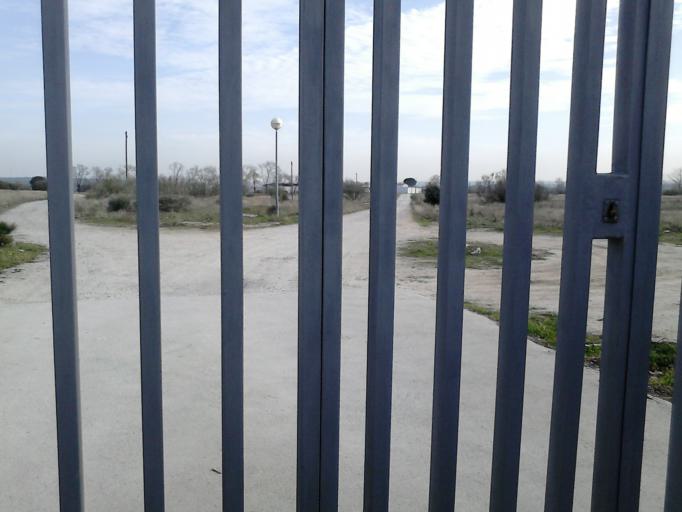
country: ES
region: Madrid
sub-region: Provincia de Madrid
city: Las Matas
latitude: 40.5492
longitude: -3.8884
